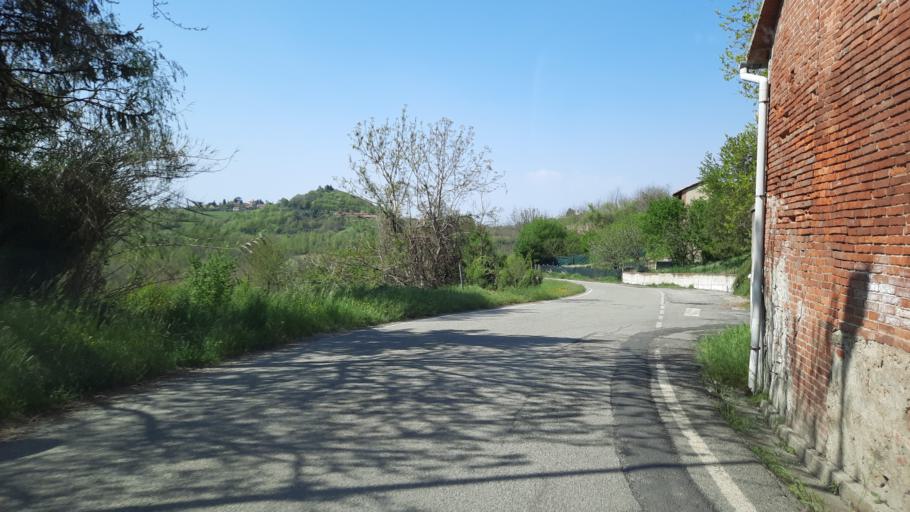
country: IT
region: Piedmont
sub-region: Provincia di Torino
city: Valentino
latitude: 45.1538
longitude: 8.1140
